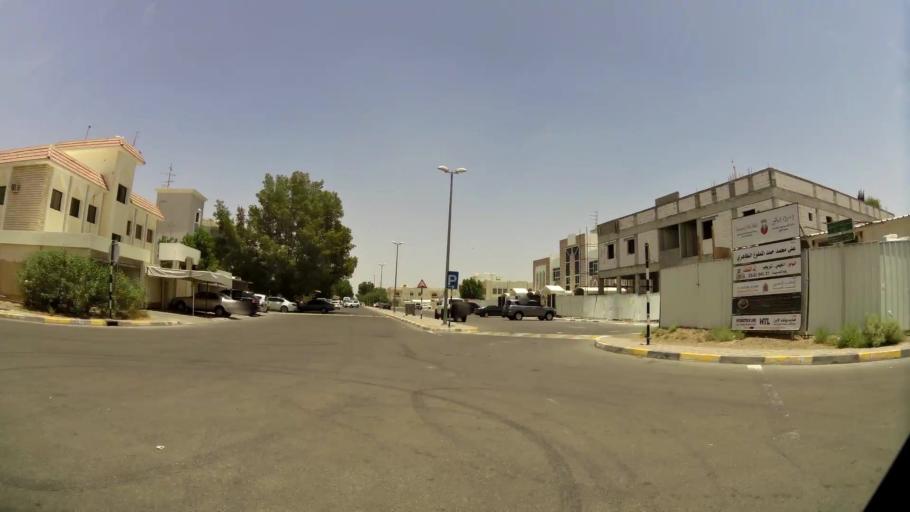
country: OM
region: Al Buraimi
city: Al Buraymi
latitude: 24.2612
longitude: 55.7223
